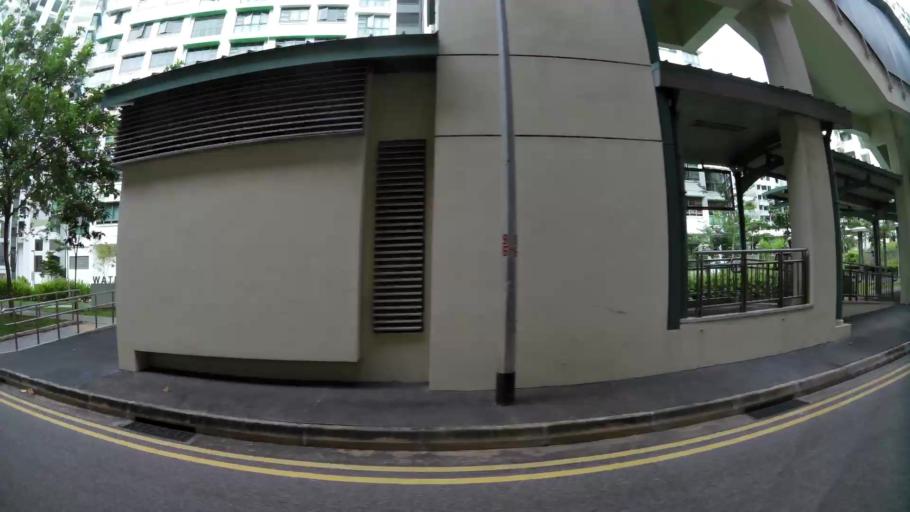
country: MY
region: Johor
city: Kampung Pasir Gudang Baru
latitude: 1.4055
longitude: 103.9087
